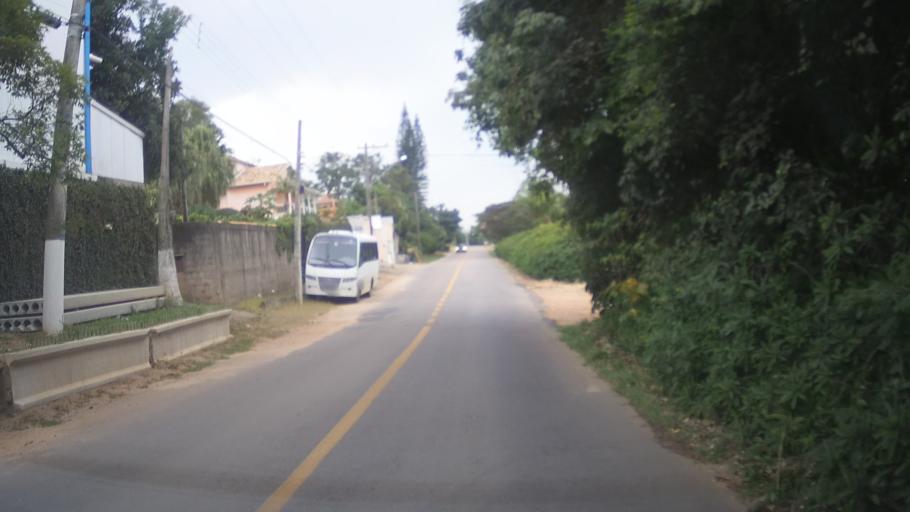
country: BR
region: Sao Paulo
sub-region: Itupeva
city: Itupeva
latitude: -23.1698
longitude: -47.0796
